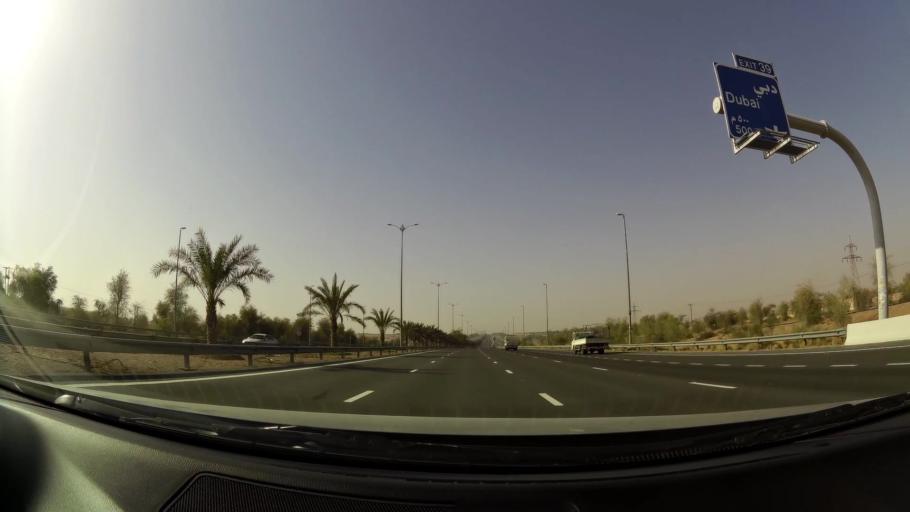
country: OM
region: Al Buraimi
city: Al Buraymi
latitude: 24.5569
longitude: 55.7532
